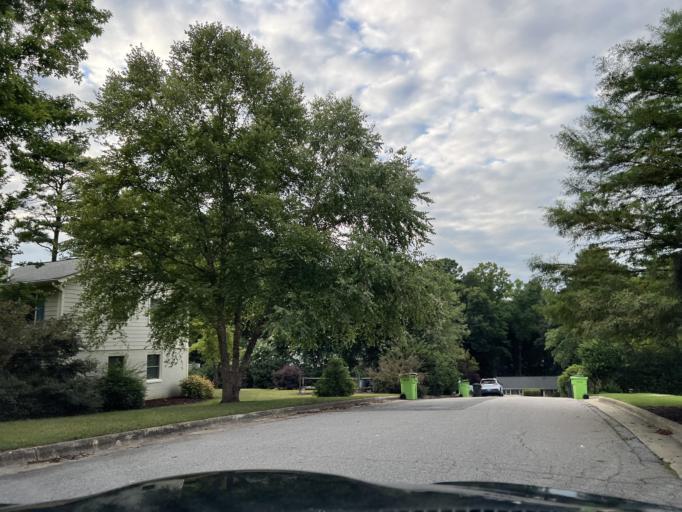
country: US
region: North Carolina
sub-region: Wake County
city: West Raleigh
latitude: 35.8603
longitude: -78.6515
